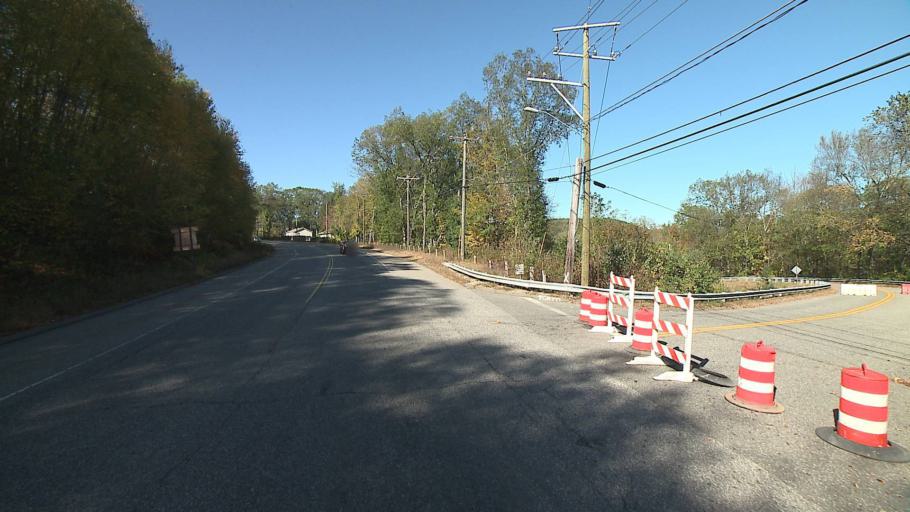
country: US
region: Connecticut
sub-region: Windham County
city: Willimantic
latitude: 41.7201
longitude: -72.2523
